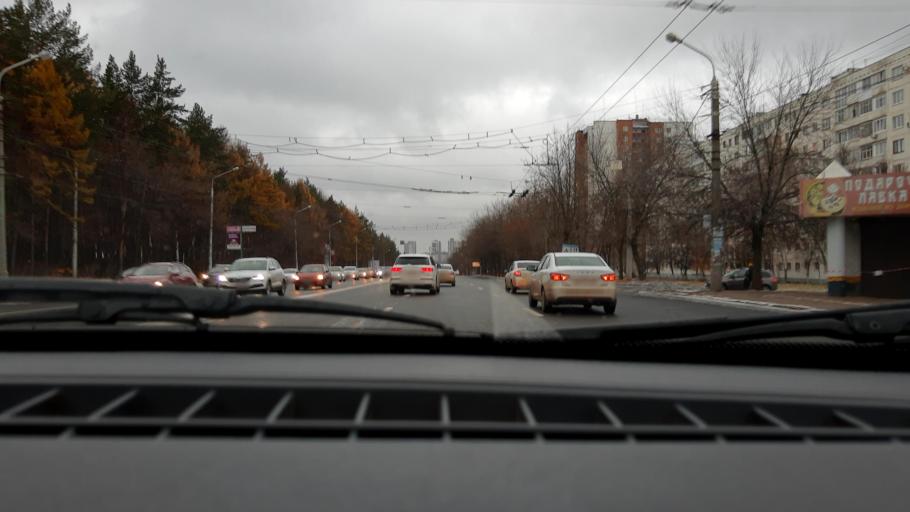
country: RU
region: Bashkortostan
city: Ufa
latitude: 54.7399
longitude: 56.0280
